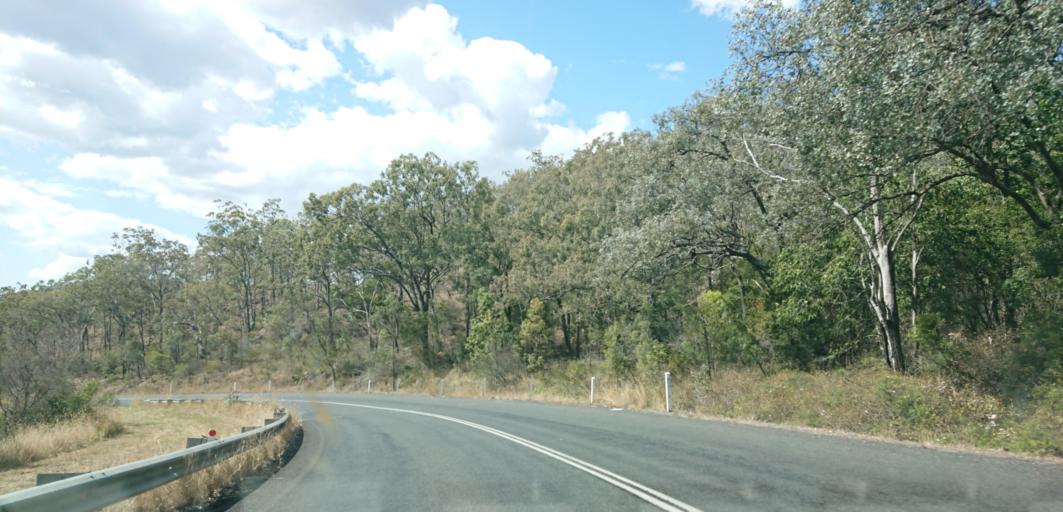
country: AU
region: Queensland
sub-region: Toowoomba
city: Top Camp
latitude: -27.8200
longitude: 152.1018
